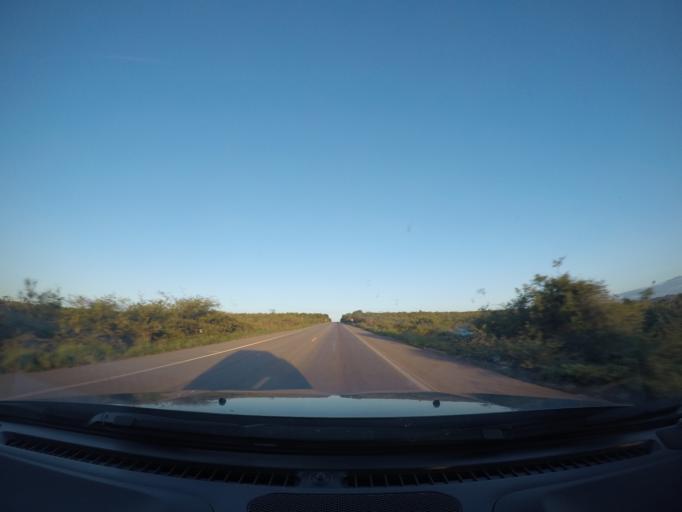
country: BR
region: Bahia
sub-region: Seabra
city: Seabra
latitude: -12.3920
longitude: -41.9147
